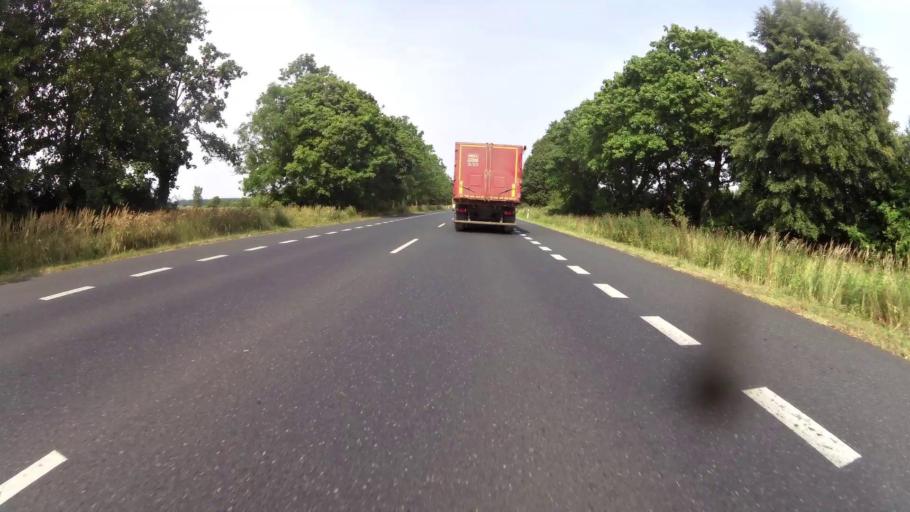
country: PL
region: West Pomeranian Voivodeship
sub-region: Powiat pyrzycki
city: Lipiany
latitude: 52.9696
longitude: 14.9709
